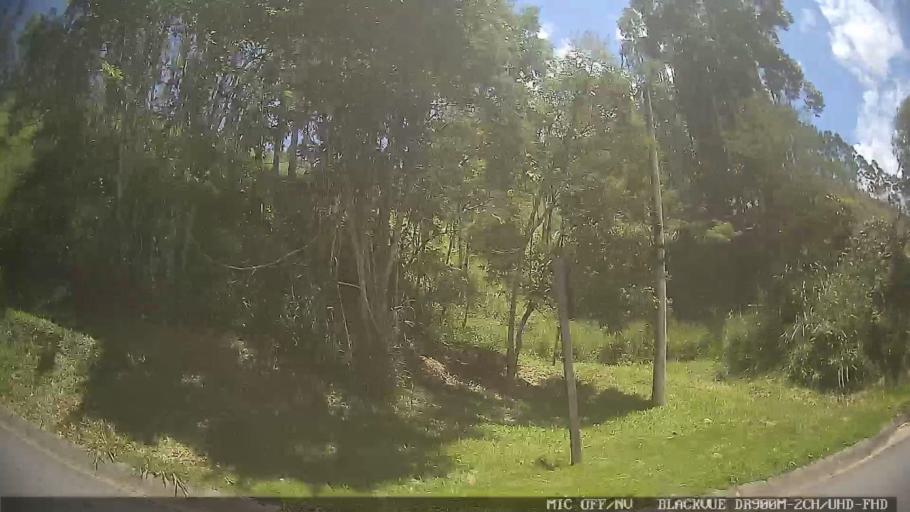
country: BR
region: Sao Paulo
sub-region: Santa Branca
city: Santa Branca
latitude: -23.3335
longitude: -45.7144
